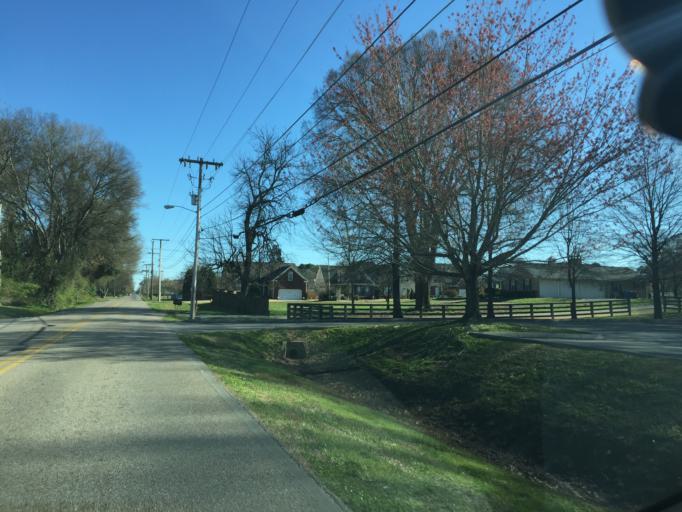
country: US
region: Tennessee
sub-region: Hamilton County
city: East Brainerd
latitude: 35.0312
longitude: -85.1744
